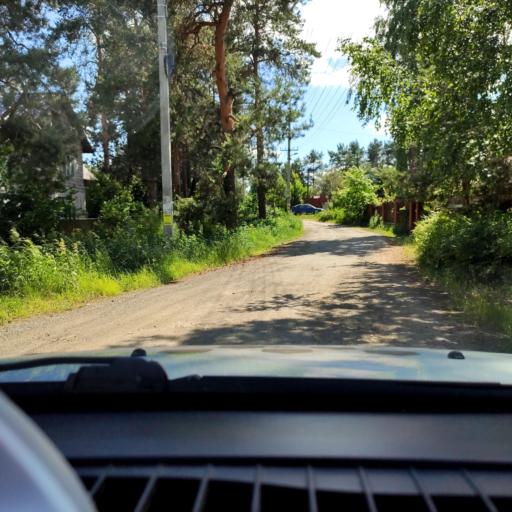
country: RU
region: Perm
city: Perm
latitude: 58.0617
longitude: 56.3077
